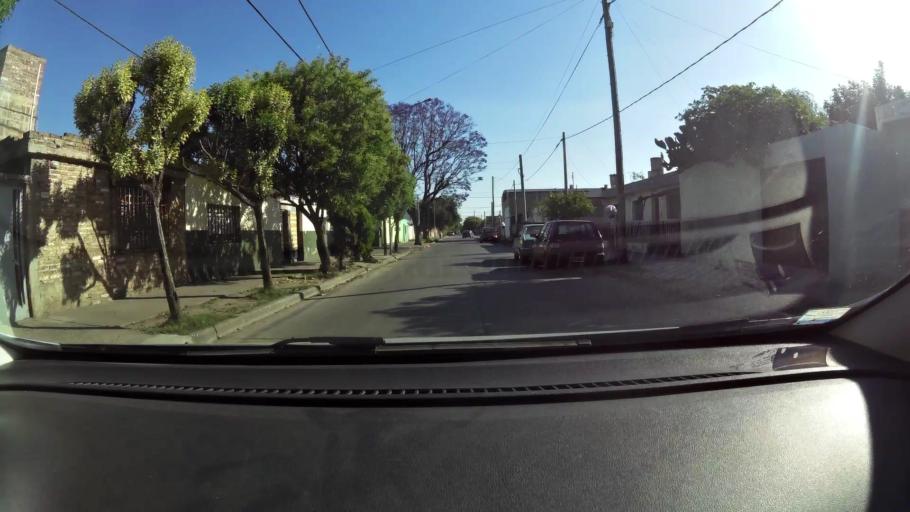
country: AR
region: Cordoba
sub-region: Departamento de Capital
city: Cordoba
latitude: -31.3869
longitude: -64.1657
